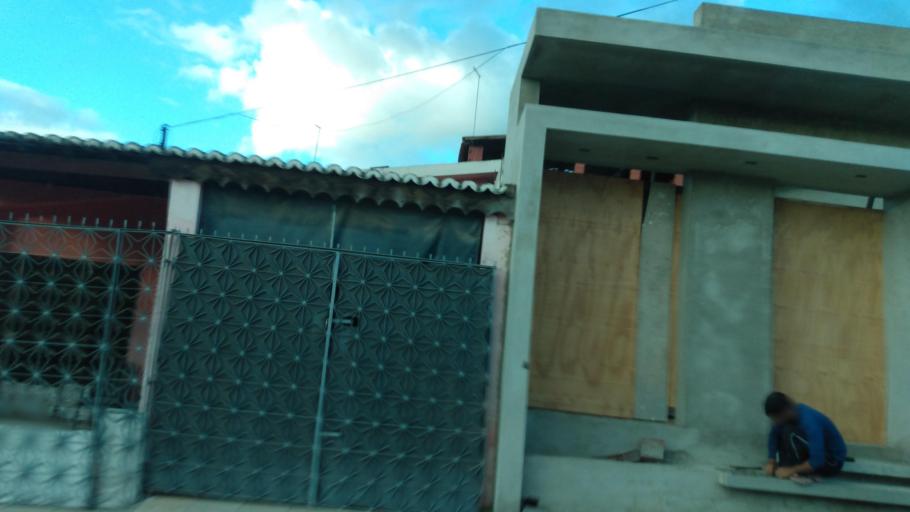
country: BR
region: Pernambuco
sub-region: Bezerros
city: Bezerros
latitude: -8.2373
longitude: -35.7506
